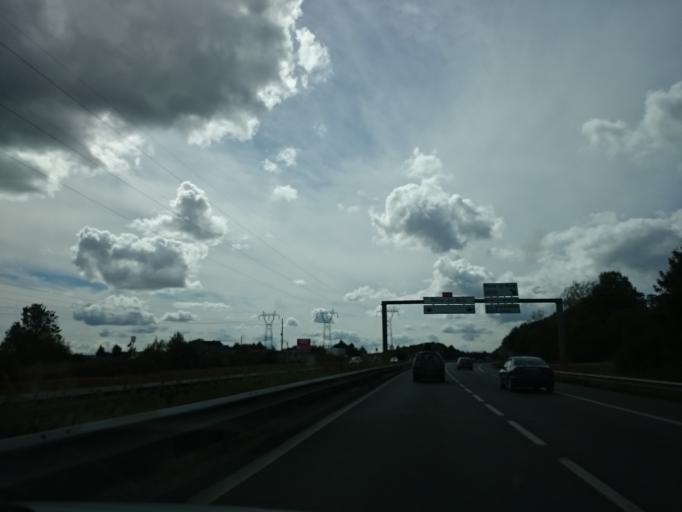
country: FR
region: Pays de la Loire
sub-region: Departement de la Loire-Atlantique
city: Les Sorinieres
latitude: 47.1597
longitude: -1.5365
